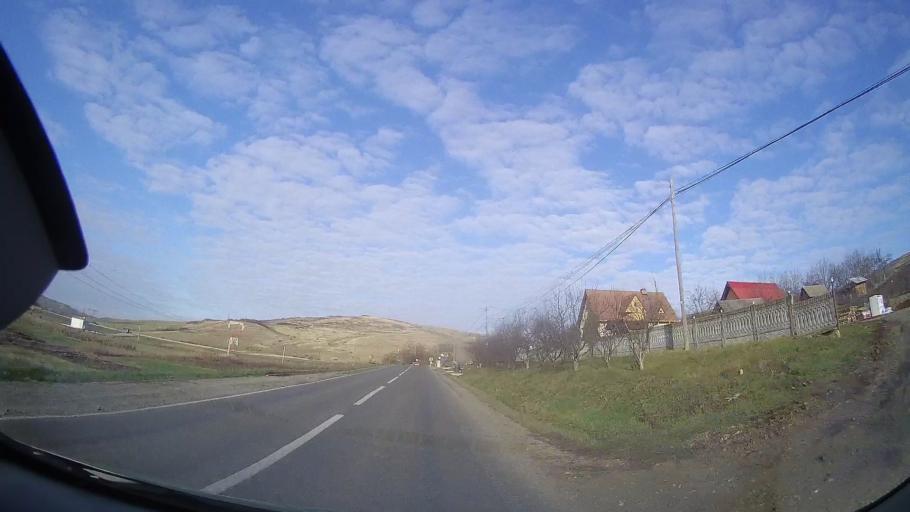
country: RO
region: Cluj
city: Caianu Mic
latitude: 46.8099
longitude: 23.8726
